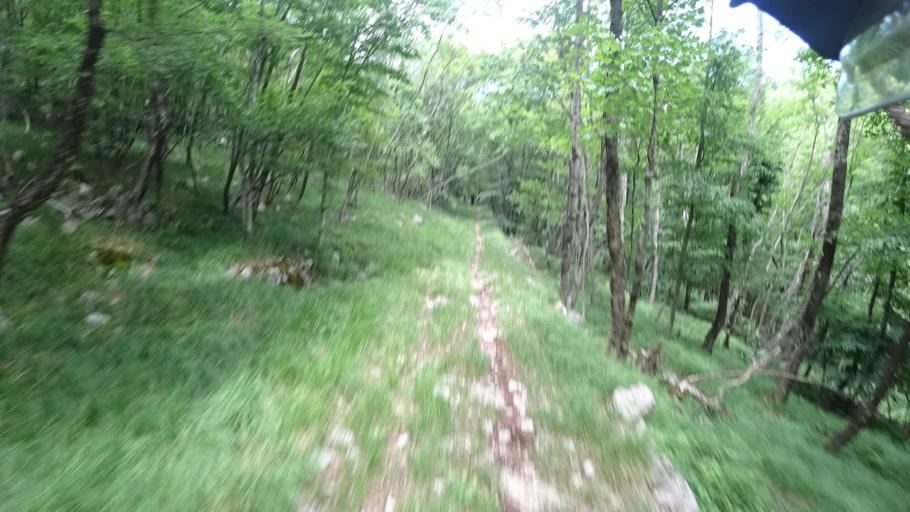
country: HR
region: Primorsko-Goranska
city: Bribir
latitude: 45.2216
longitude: 14.7406
